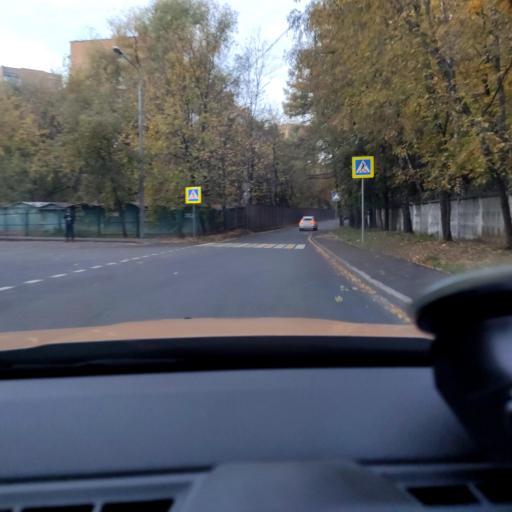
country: RU
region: Moscow
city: Vatutino
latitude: 55.8614
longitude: 37.7005
